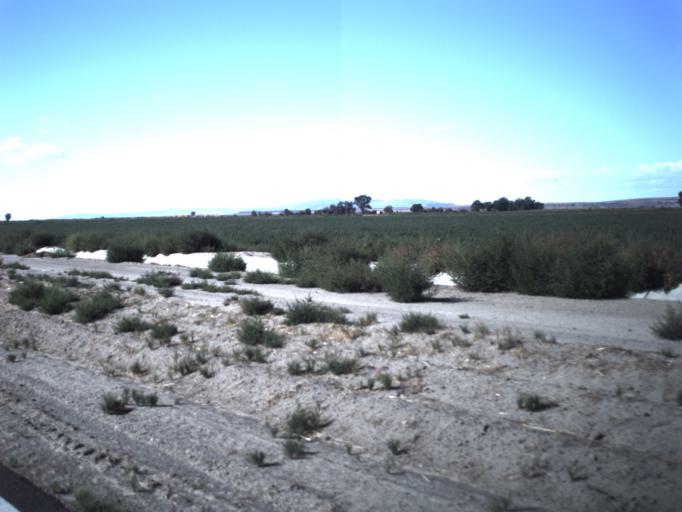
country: US
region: Utah
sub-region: Millard County
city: Delta
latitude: 39.2700
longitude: -112.6531
